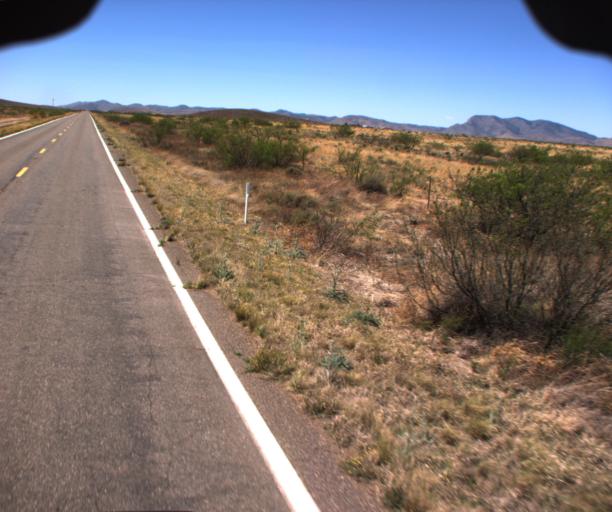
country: US
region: Arizona
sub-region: Cochise County
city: Douglas
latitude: 31.6403
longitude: -109.1780
